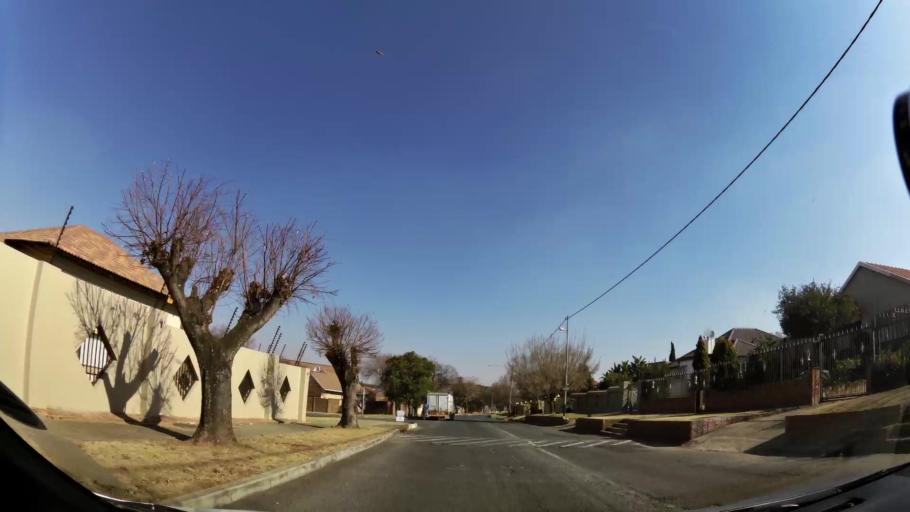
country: ZA
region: Gauteng
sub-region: City of Johannesburg Metropolitan Municipality
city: Johannesburg
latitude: -26.2612
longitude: 28.0664
